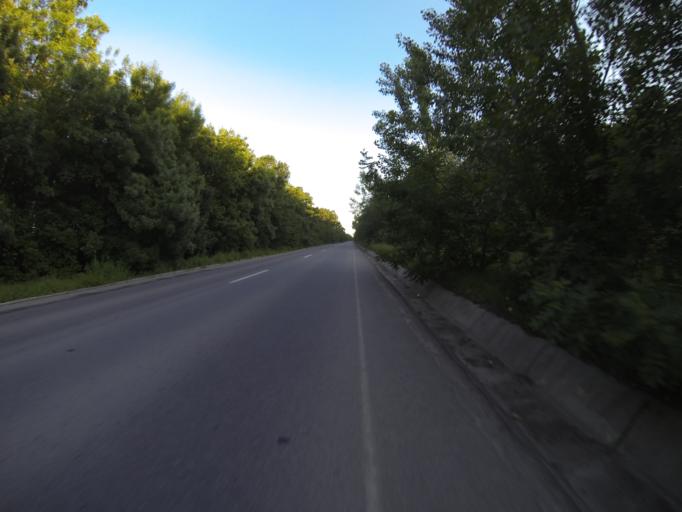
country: RO
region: Dolj
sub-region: Comuna Caloparu
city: Calopar
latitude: 44.1577
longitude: 23.7437
